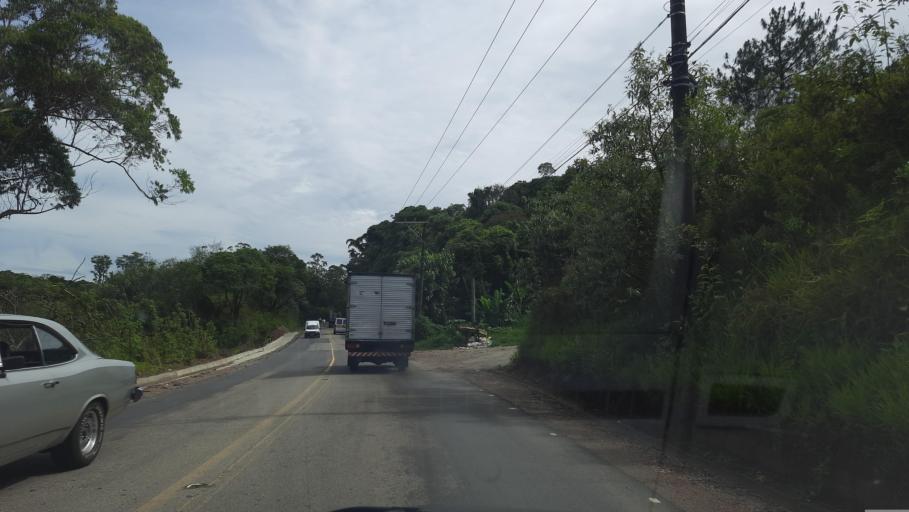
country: BR
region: Sao Paulo
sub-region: Franco Da Rocha
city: Franco da Rocha
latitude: -23.3506
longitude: -46.6639
